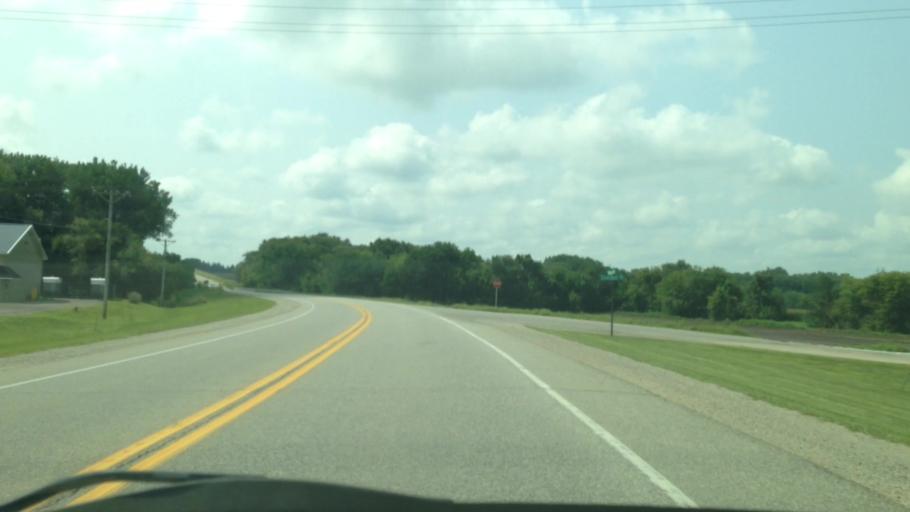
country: US
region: Iowa
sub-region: Linn County
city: Fairfax
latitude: 41.9257
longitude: -91.7835
